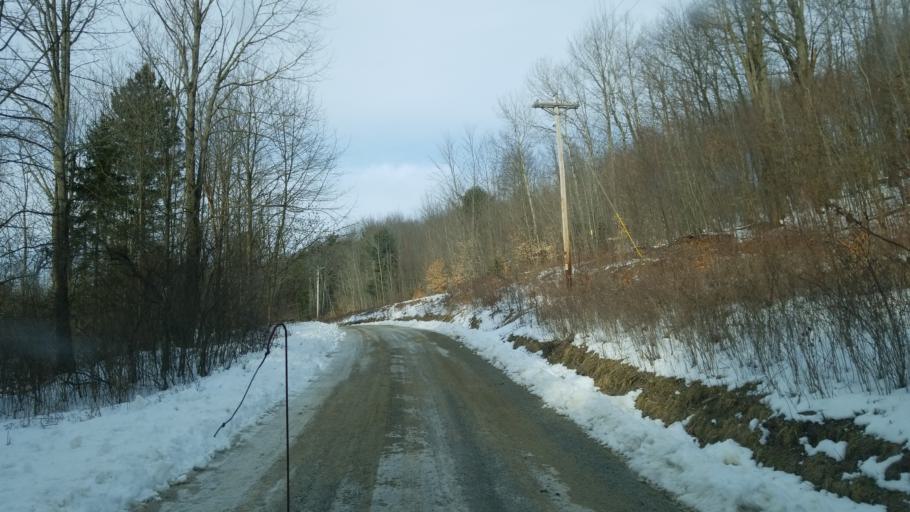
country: US
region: Pennsylvania
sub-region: Tioga County
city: Westfield
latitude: 41.9605
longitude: -77.7156
